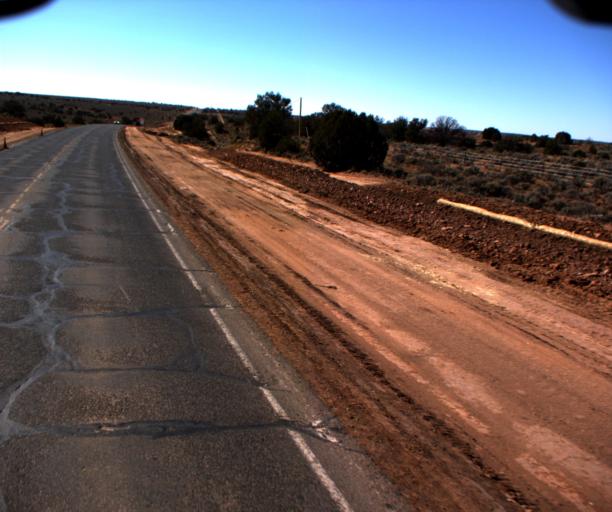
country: US
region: Arizona
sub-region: Apache County
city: Ganado
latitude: 35.7124
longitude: -109.4925
